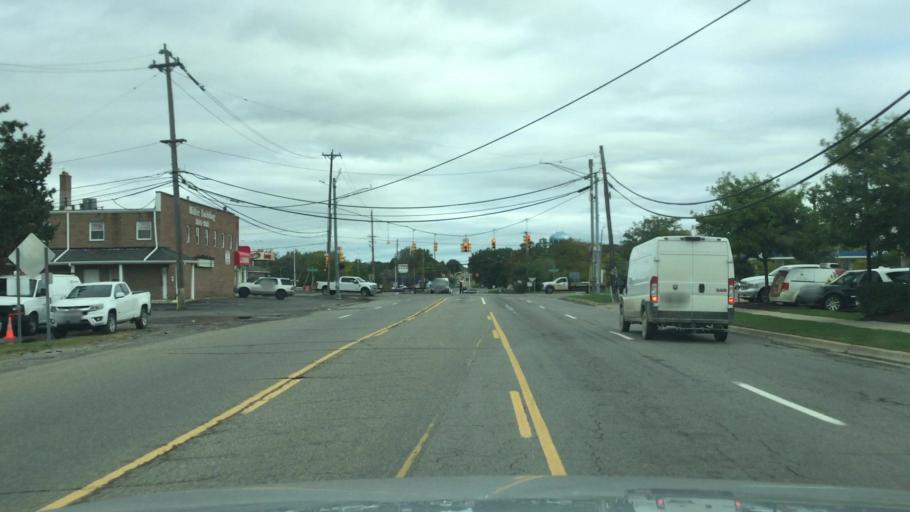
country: US
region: Michigan
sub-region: Oakland County
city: Keego Harbor
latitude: 42.6383
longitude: -83.3554
